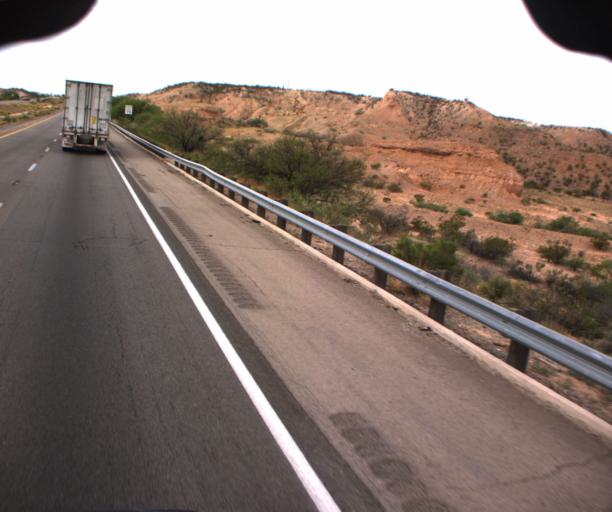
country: US
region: Arizona
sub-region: Cochise County
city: Benson
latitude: 31.9753
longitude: -110.3191
